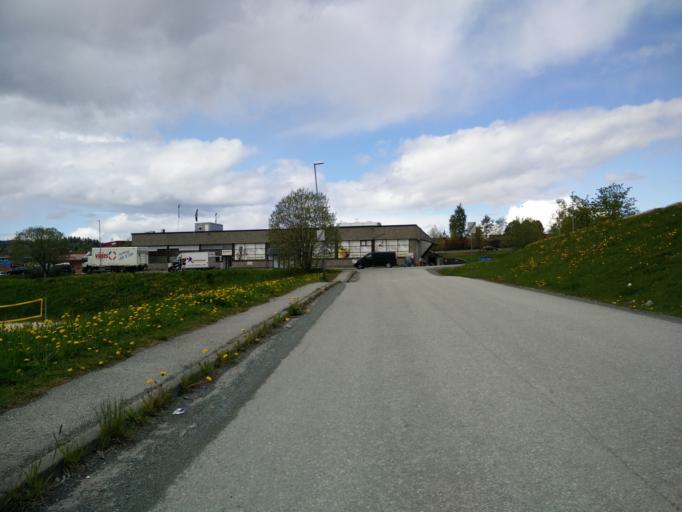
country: NO
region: Sor-Trondelag
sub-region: Trondheim
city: Trondheim
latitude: 63.4006
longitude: 10.4064
